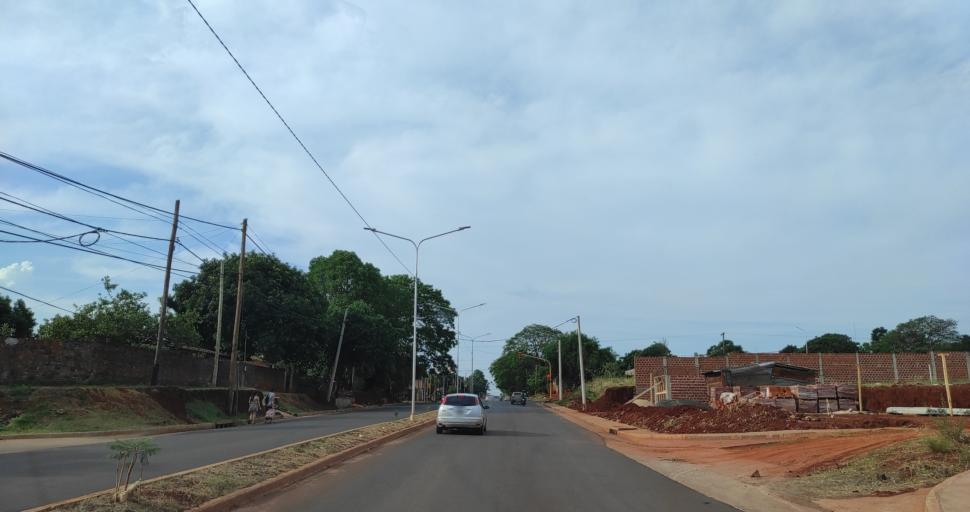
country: AR
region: Misiones
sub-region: Departamento de Capital
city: Posadas
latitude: -27.3924
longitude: -55.9276
